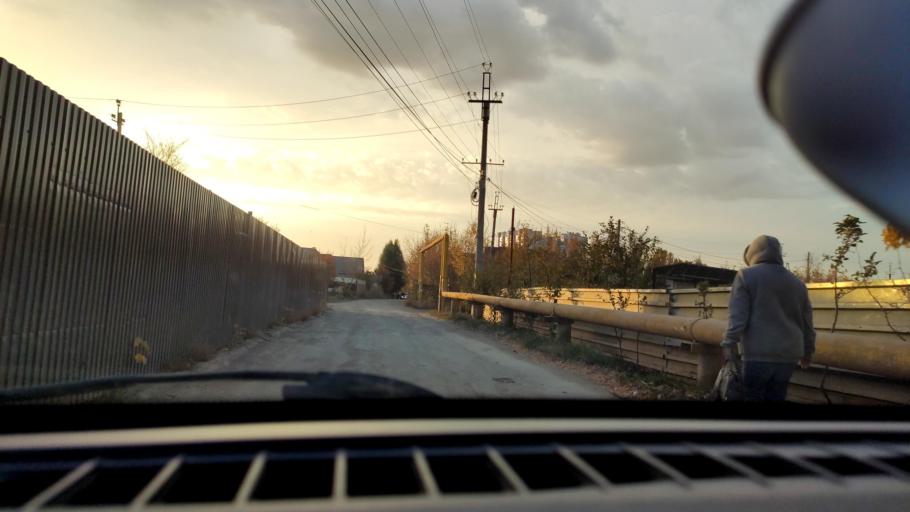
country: RU
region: Samara
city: Samara
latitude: 53.2730
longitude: 50.2283
